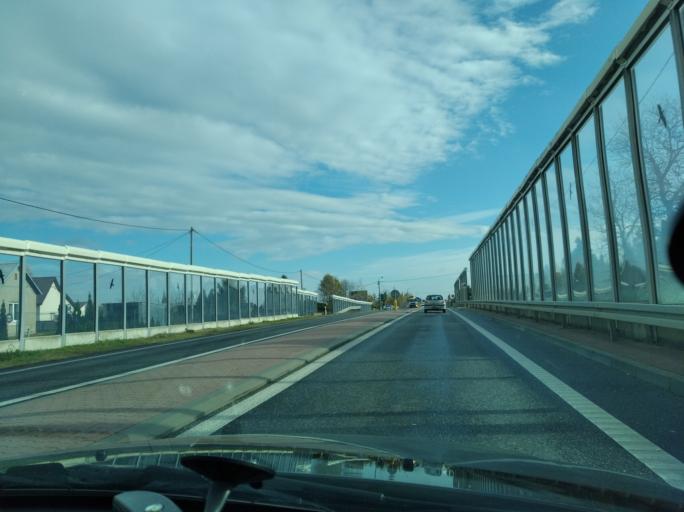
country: PL
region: Subcarpathian Voivodeship
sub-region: Powiat debicki
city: Brzeznica
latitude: 50.0625
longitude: 21.5165
